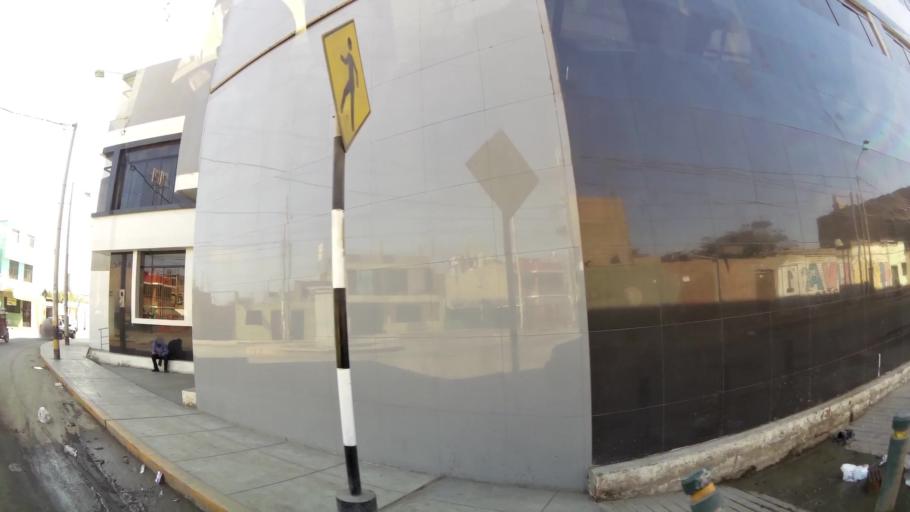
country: PE
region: Ica
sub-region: Provincia de Chincha
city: Chincha Alta
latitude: -13.4156
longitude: -76.1285
